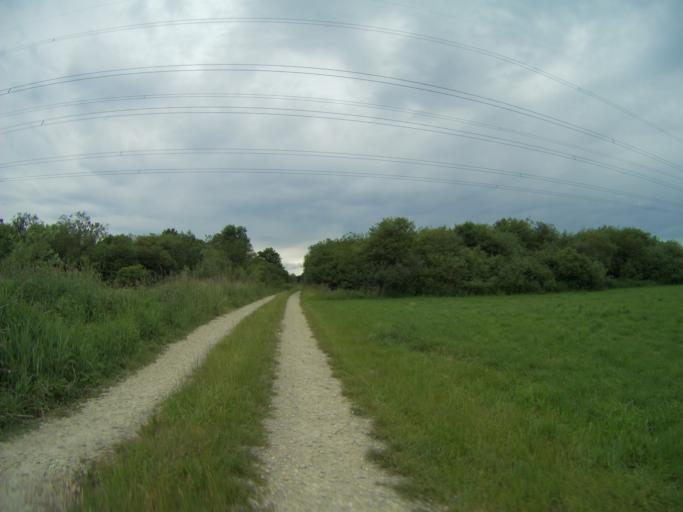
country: DE
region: Bavaria
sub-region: Upper Bavaria
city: Langenbach
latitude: 48.4020
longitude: 11.8731
